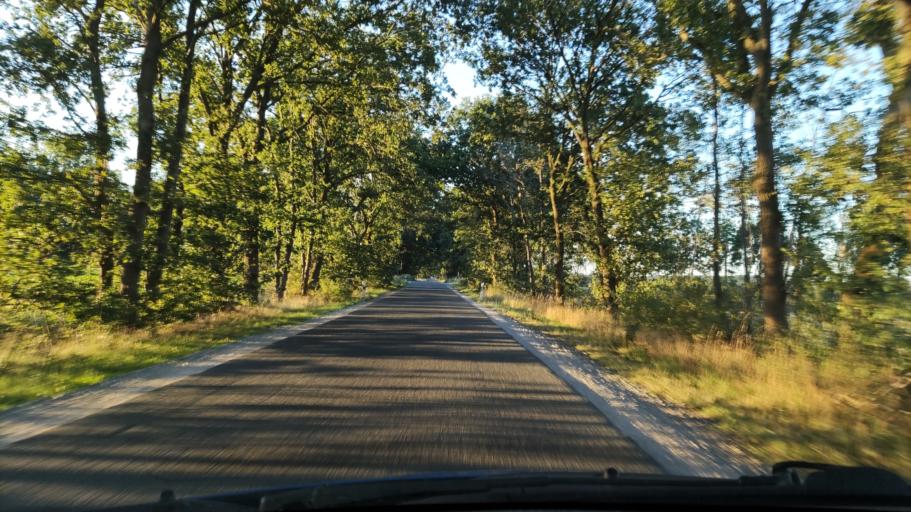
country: DE
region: Lower Saxony
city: Klein Gusborn
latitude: 53.0716
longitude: 11.1905
